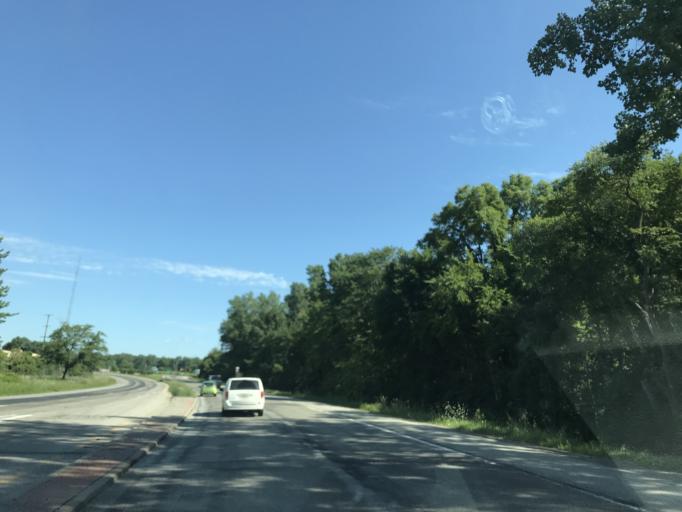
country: US
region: Michigan
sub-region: Kalamazoo County
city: Eastwood
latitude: 42.2811
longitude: -85.5527
